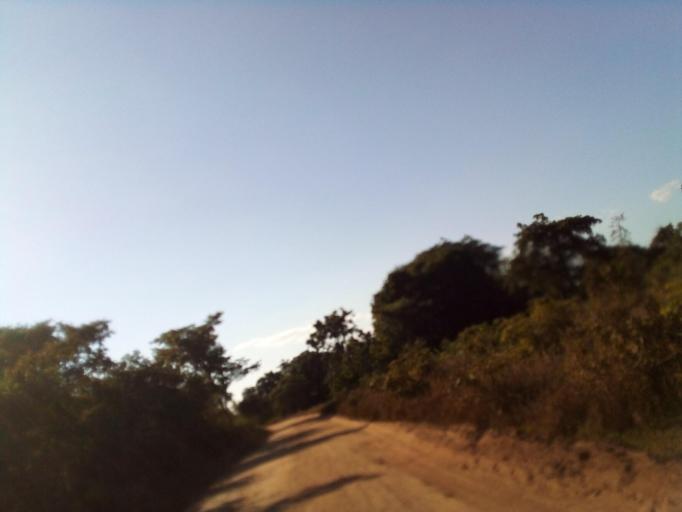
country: MZ
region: Zambezia
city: Quelimane
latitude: -17.4796
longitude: 36.5423
